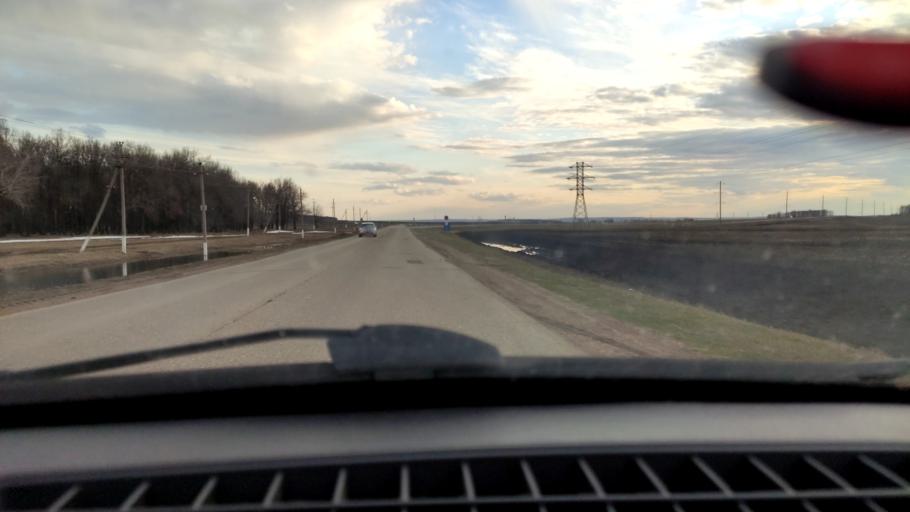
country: RU
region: Bashkortostan
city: Tolbazy
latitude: 53.9979
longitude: 55.8544
